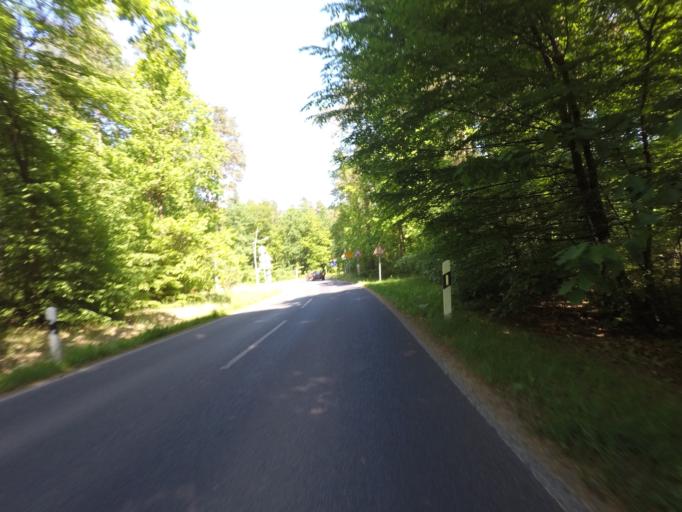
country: DE
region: Brandenburg
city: Eberswalde
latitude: 52.8246
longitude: 13.7780
